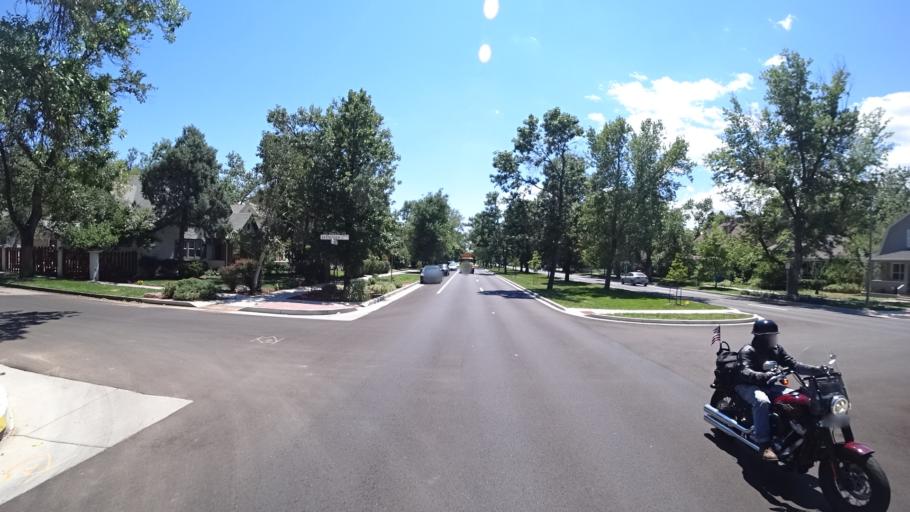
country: US
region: Colorado
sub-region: El Paso County
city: Colorado Springs
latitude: 38.8631
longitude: -104.8200
